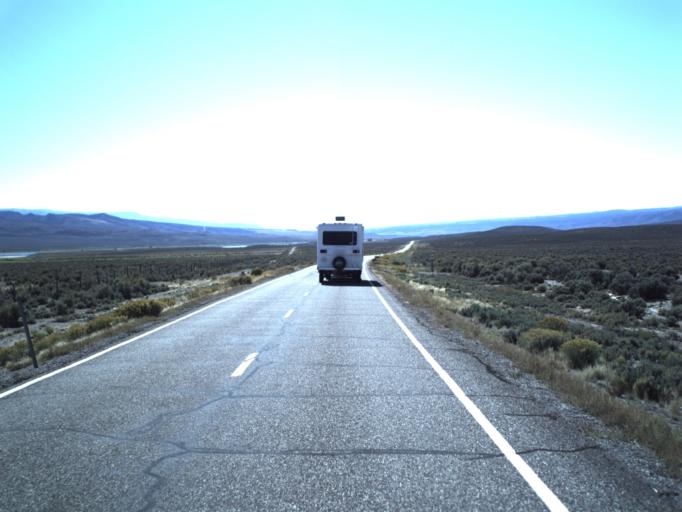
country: US
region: Utah
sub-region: Piute County
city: Junction
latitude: 38.2578
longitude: -111.9862
